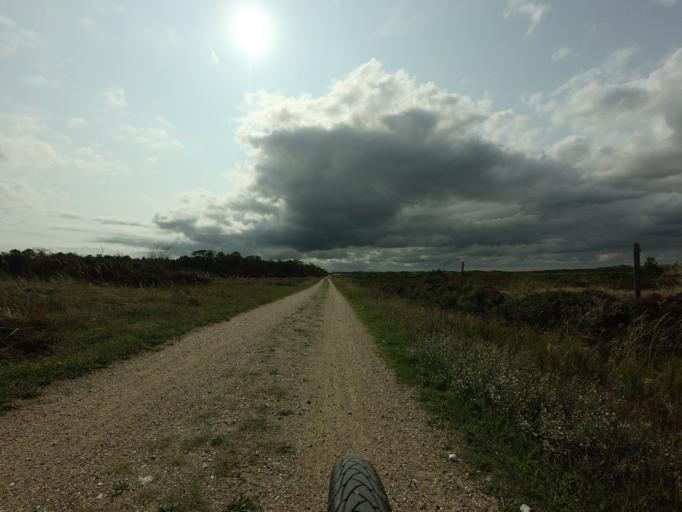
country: DK
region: North Denmark
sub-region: Frederikshavn Kommune
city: Strandby
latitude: 57.6395
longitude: 10.4004
